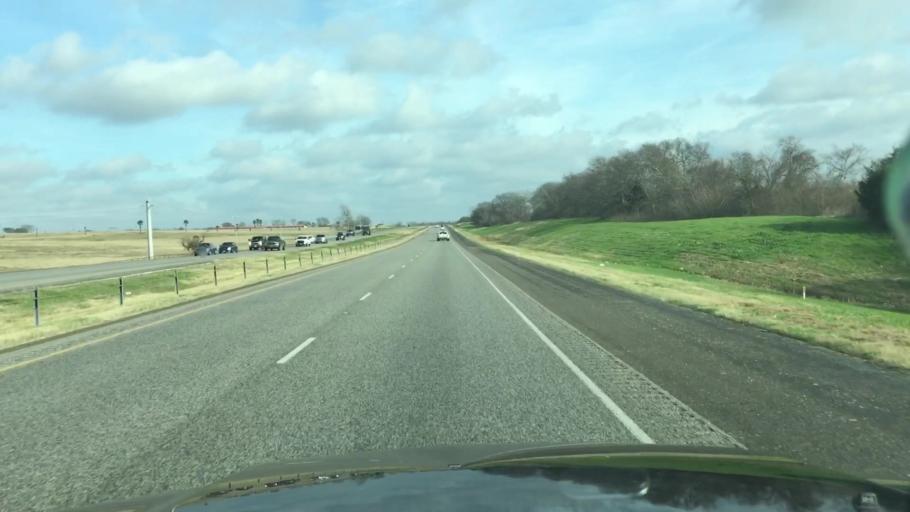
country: US
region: Texas
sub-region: Washington County
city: Brenham
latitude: 30.1369
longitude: -96.3464
